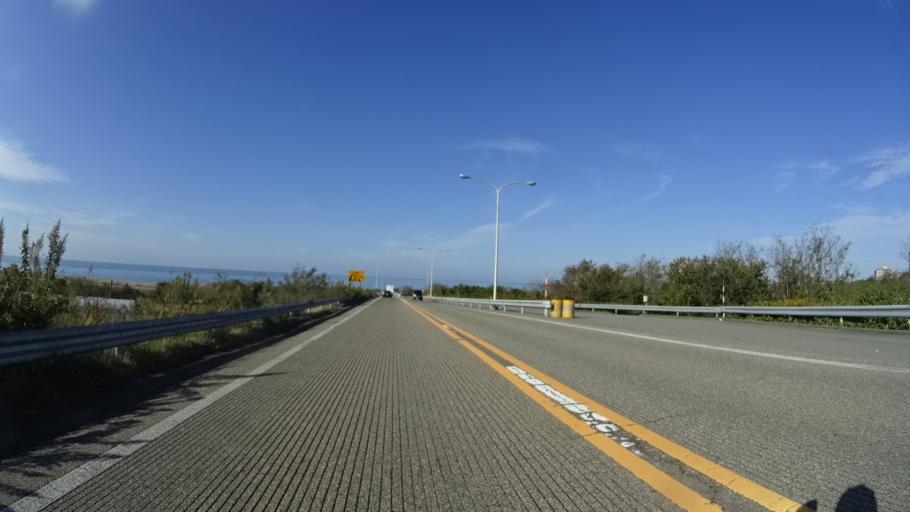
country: JP
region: Ishikawa
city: Kanazawa-shi
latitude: 36.6481
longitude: 136.6363
